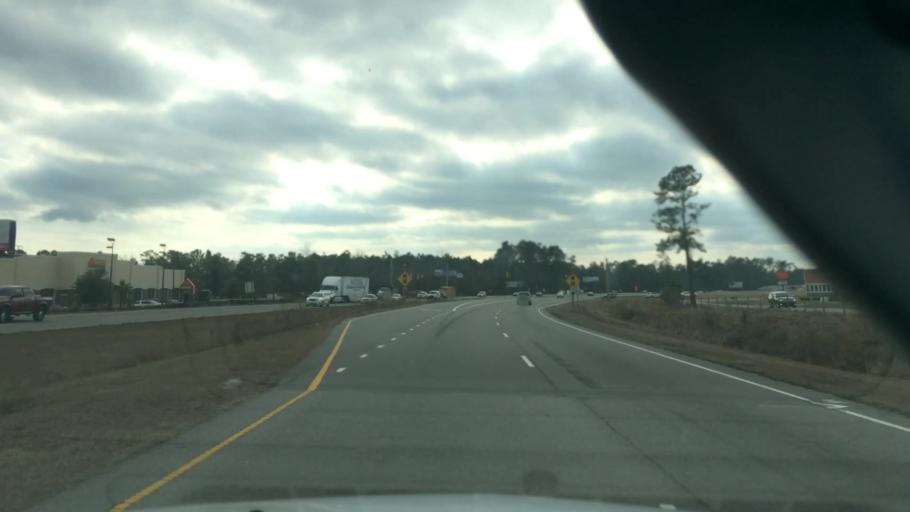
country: US
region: North Carolina
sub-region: Brunswick County
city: Shallotte
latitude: 33.9629
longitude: -78.4165
